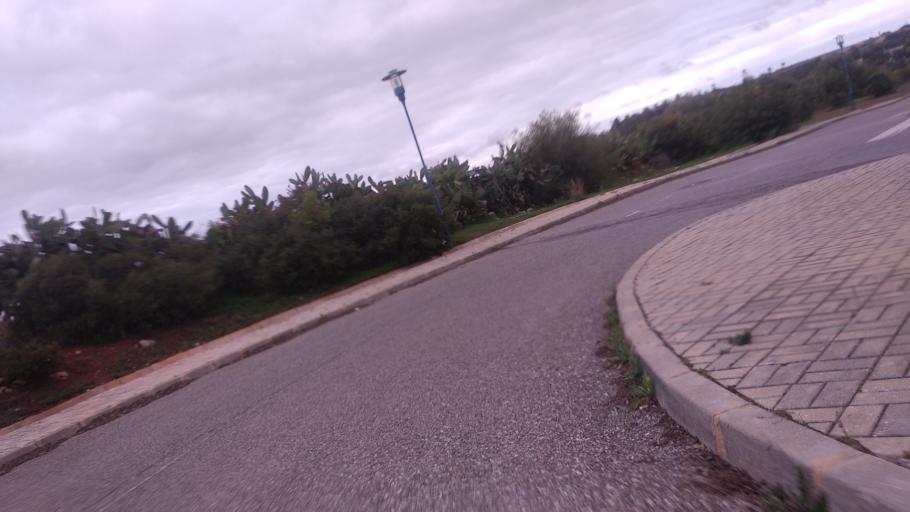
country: PT
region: Faro
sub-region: Faro
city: Santa Barbara de Nexe
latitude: 37.0900
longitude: -7.9728
